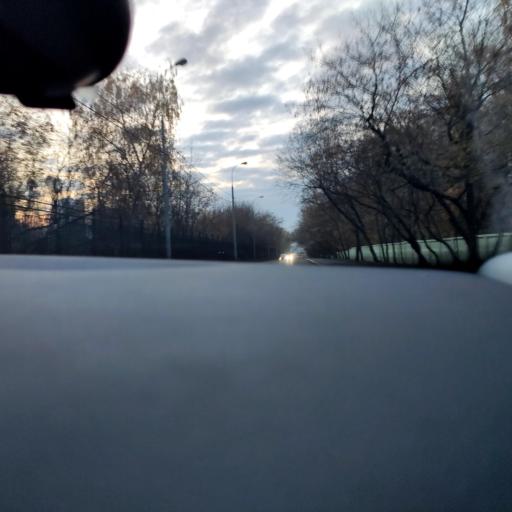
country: RU
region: Moscow
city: Kuz'minki
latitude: 55.6794
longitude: 37.7904
